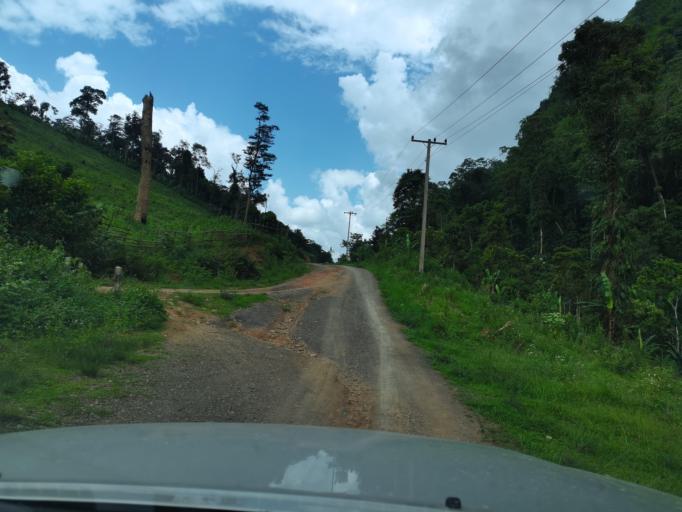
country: LA
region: Loungnamtha
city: Muang Long
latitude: 20.7789
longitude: 101.0166
